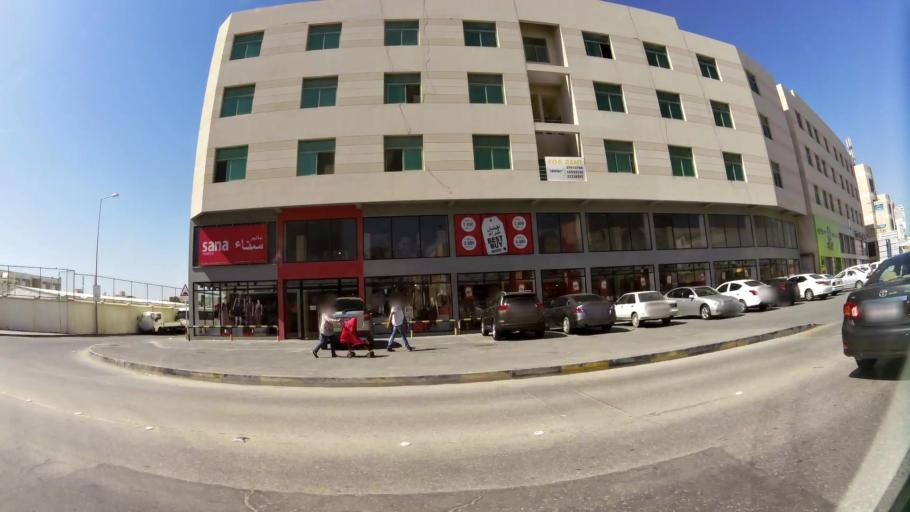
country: BH
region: Muharraq
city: Al Muharraq
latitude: 26.2608
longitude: 50.6192
